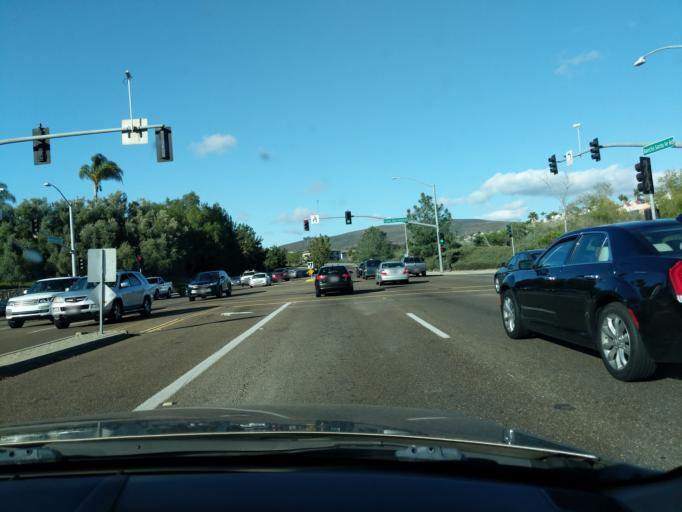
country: US
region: California
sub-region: San Diego County
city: Encinitas
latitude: 33.0720
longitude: -117.2427
